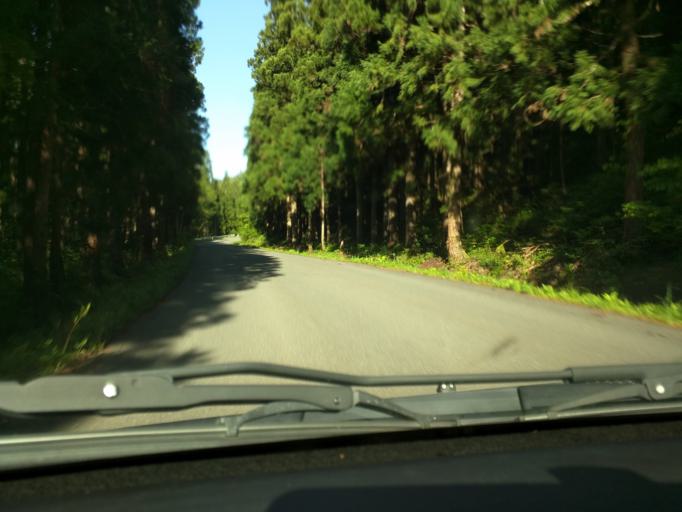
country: JP
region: Fukushima
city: Kitakata
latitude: 37.4846
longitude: 139.6659
